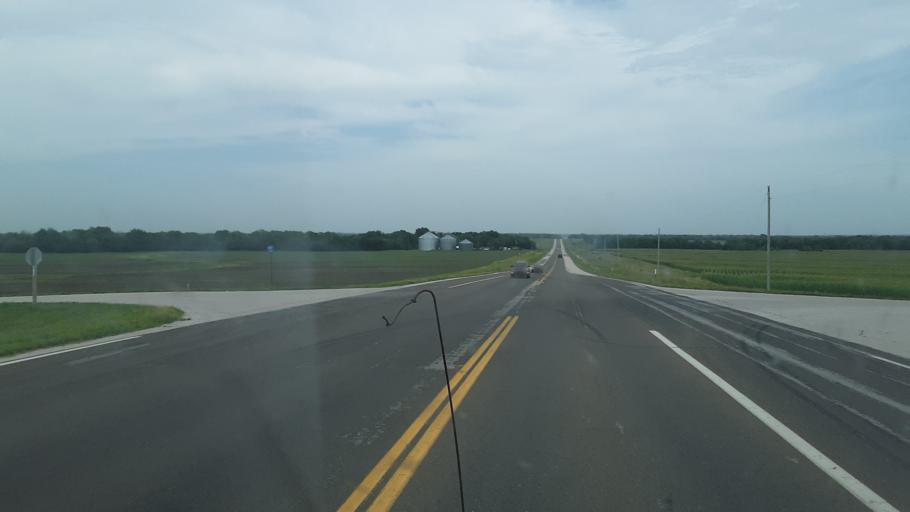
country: US
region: Kansas
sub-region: Allen County
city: Iola
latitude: 37.9220
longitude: -95.4829
